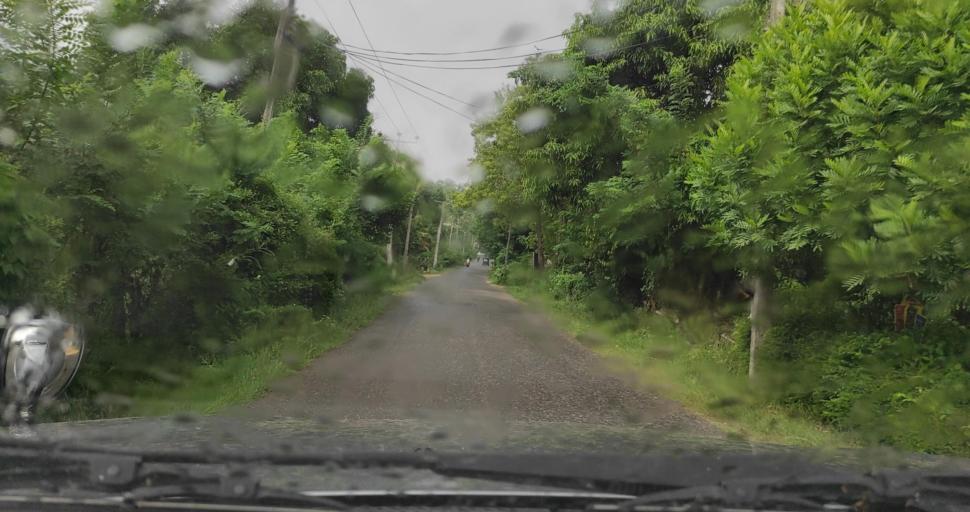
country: LK
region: Eastern Province
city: Trincomalee
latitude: 8.3672
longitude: 81.0077
